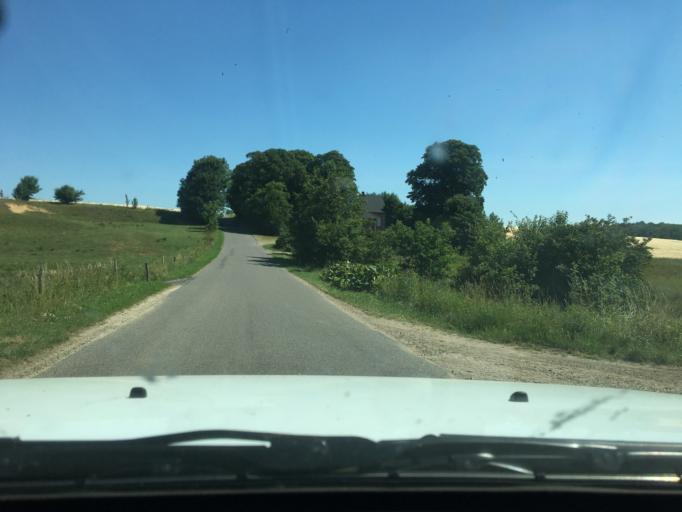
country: DK
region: Central Jutland
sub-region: Horsens Kommune
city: Braedstrup
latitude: 55.9361
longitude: 9.5408
